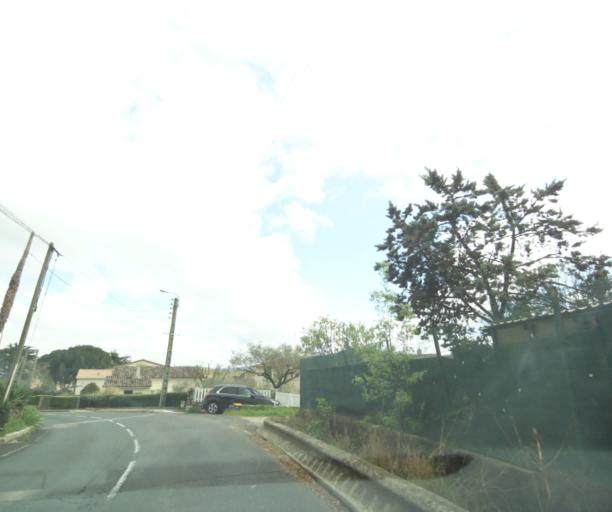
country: FR
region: Languedoc-Roussillon
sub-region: Departement de l'Herault
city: Pignan
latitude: 43.5853
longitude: 3.7561
